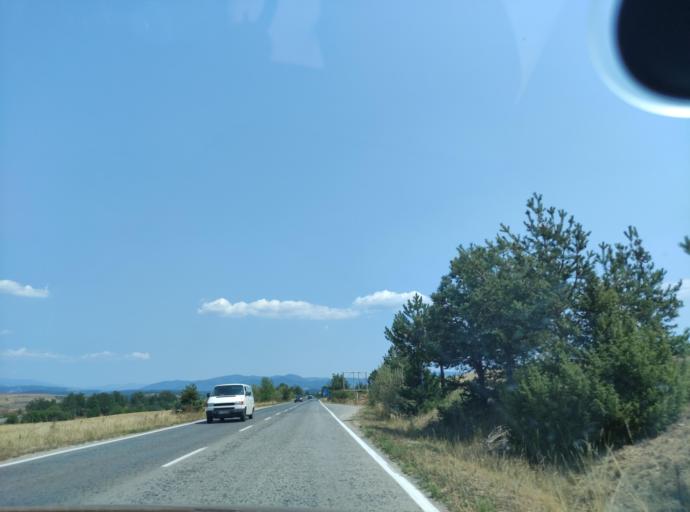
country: BG
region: Blagoevgrad
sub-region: Obshtina Razlog
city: Razlog
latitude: 41.8844
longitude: 23.4959
